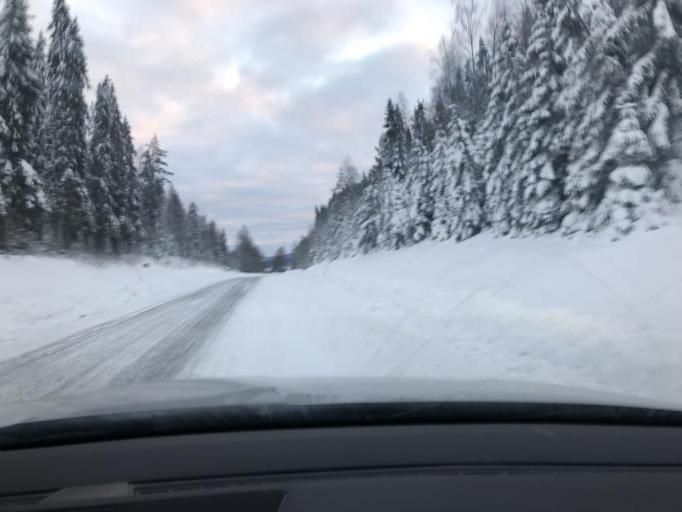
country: SE
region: Vaesternorrland
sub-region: Kramfors Kommun
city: Nordingra
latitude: 62.9788
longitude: 18.2594
